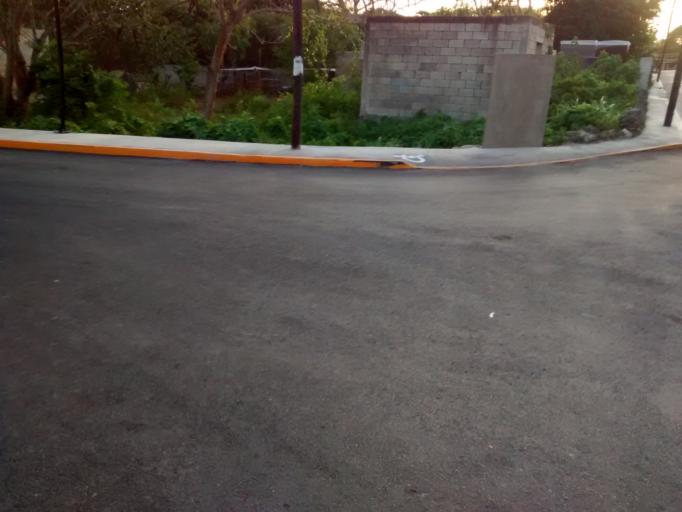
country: MX
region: Yucatan
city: Valladolid
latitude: 20.6841
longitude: -88.1930
